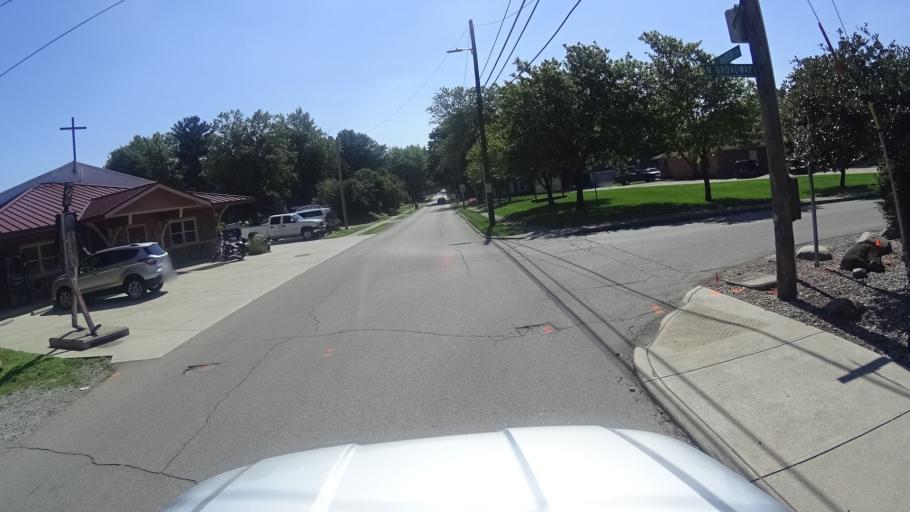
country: US
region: Indiana
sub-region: Madison County
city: Pendleton
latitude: 40.0037
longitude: -85.7446
